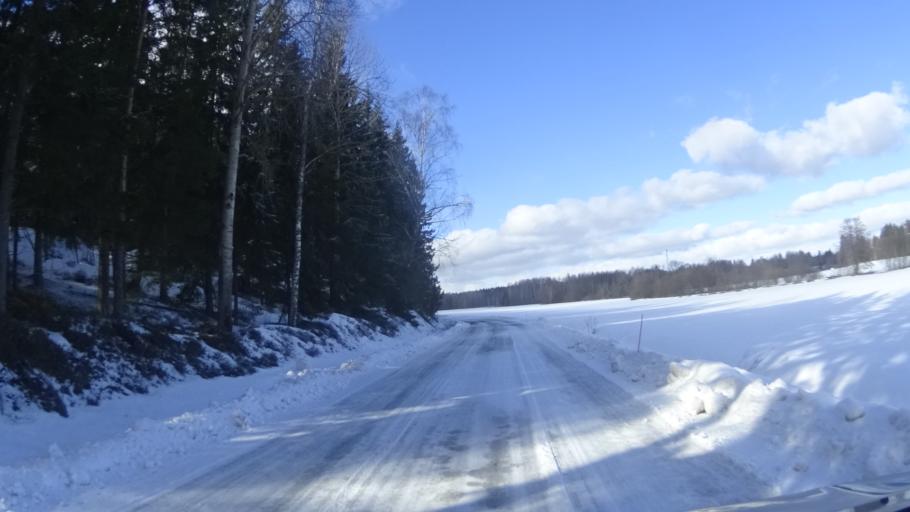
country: FI
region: Uusimaa
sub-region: Helsinki
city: Vantaa
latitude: 60.2451
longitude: 25.1744
